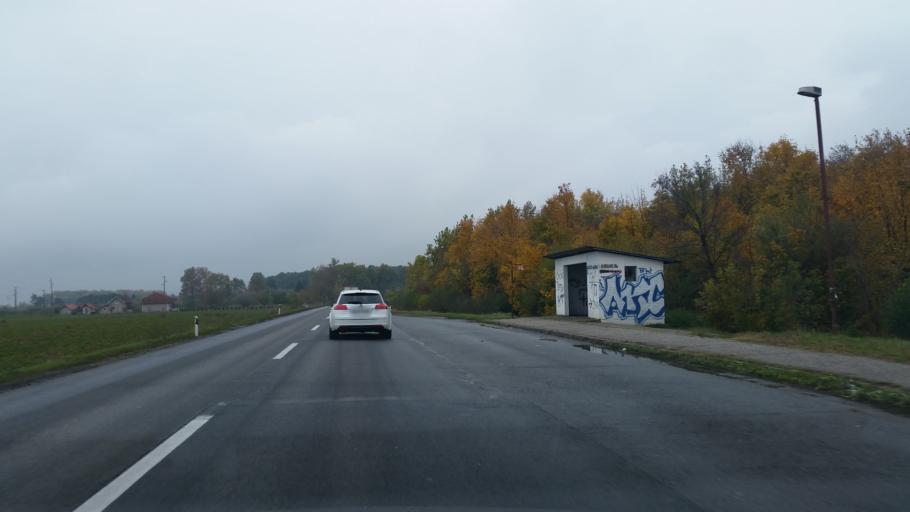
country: RS
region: Central Serbia
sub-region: Belgrade
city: Zemun
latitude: 44.9215
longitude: 20.4381
